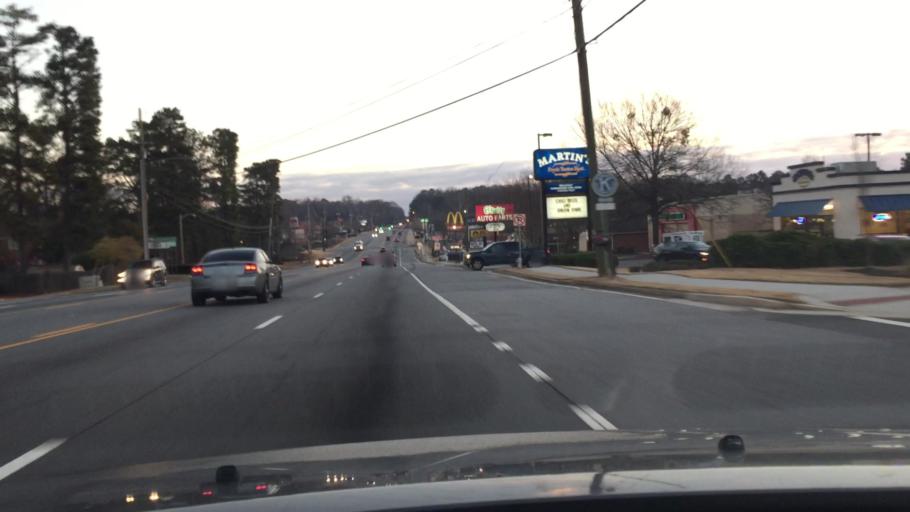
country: US
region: Georgia
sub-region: Cobb County
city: Fair Oaks
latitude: 33.9227
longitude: -84.5771
